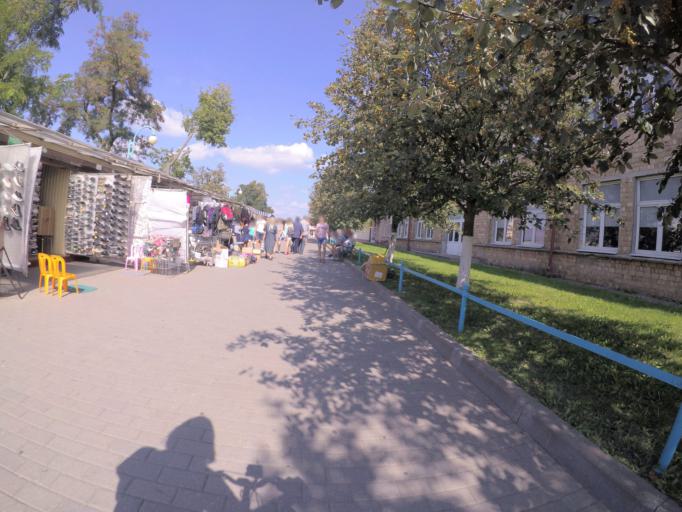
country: BY
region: Grodnenskaya
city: Hrodna
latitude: 53.6738
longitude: 23.8390
